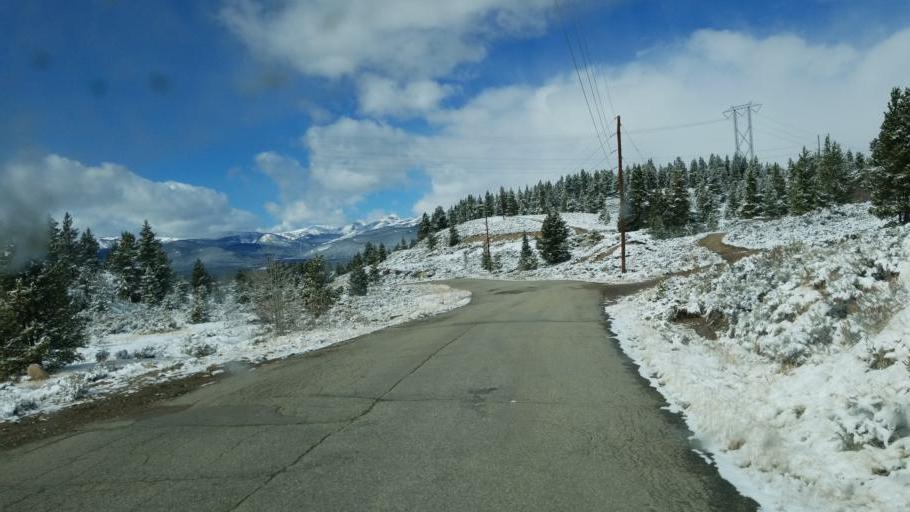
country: US
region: Colorado
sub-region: Lake County
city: Leadville
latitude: 39.2525
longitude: -106.2759
